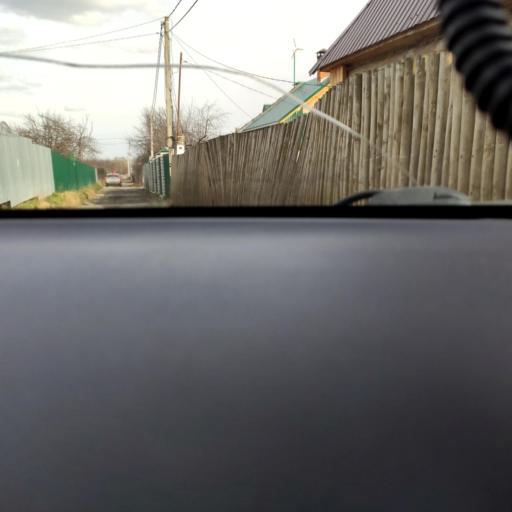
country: RU
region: Tatarstan
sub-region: Gorod Kazan'
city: Kazan
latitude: 55.8873
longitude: 49.0677
